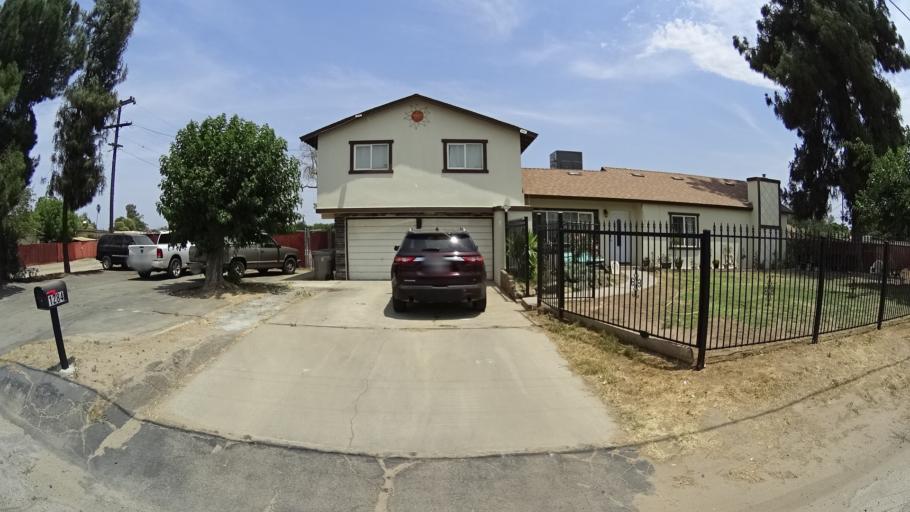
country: US
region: California
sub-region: Fresno County
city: West Park
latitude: 36.7552
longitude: -119.8532
